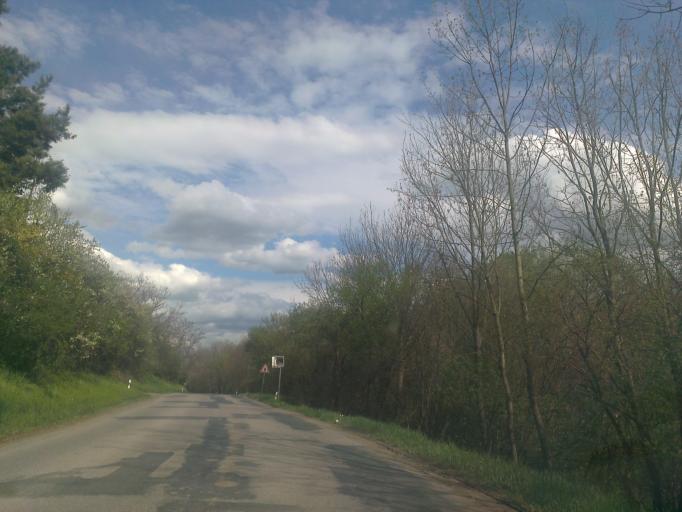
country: CZ
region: South Moravian
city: Zelesice
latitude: 49.1142
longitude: 16.5656
